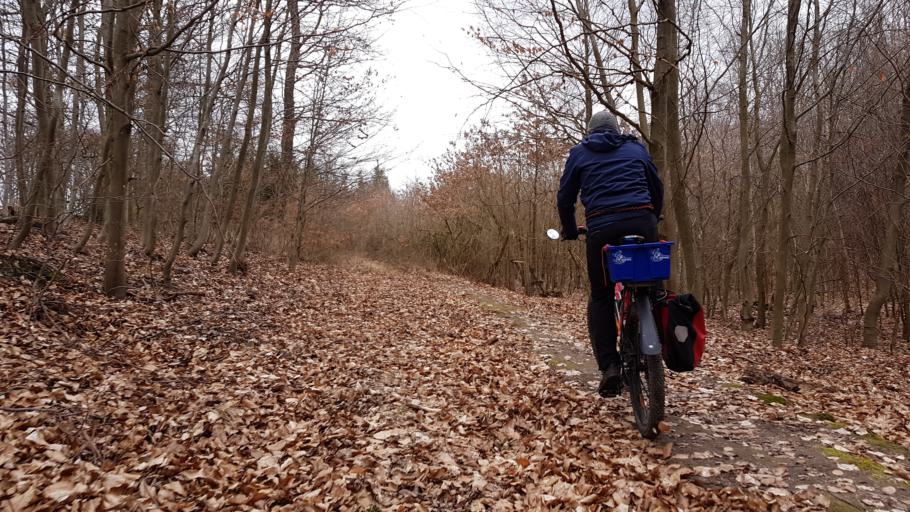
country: PL
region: West Pomeranian Voivodeship
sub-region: Powiat pyrzycki
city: Kozielice
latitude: 53.0714
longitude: 14.7513
